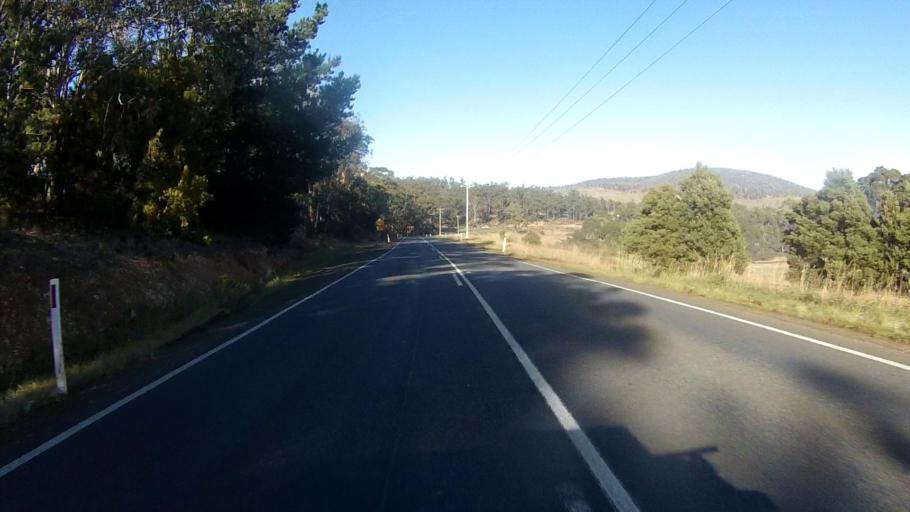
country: AU
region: Tasmania
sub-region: Sorell
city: Sorell
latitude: -42.8265
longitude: 147.8061
